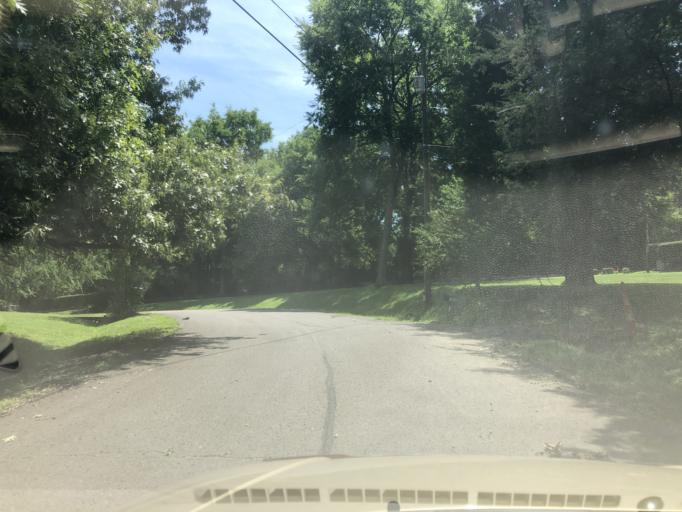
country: US
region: Tennessee
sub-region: Davidson County
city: Lakewood
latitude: 36.2466
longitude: -86.6837
